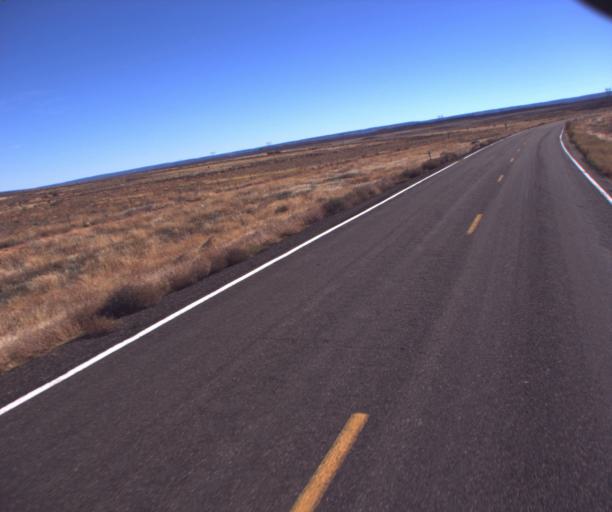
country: US
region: Arizona
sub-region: Coconino County
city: Fredonia
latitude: 36.9217
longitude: -112.4416
